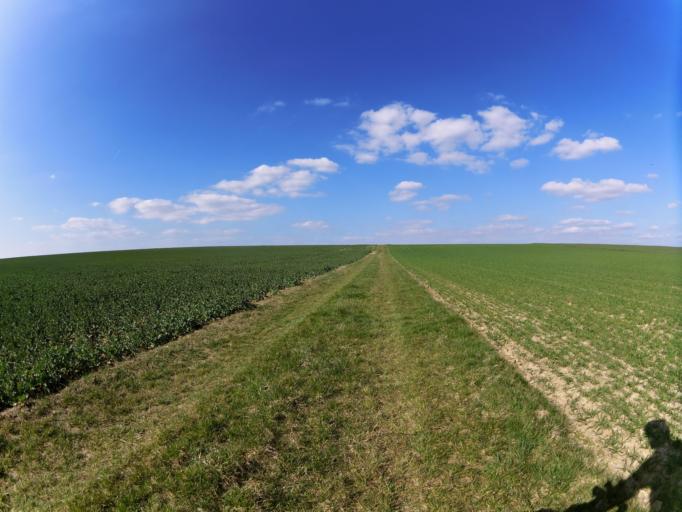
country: DE
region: Bavaria
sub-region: Regierungsbezirk Unterfranken
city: Dettelbach
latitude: 49.8348
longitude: 10.1612
